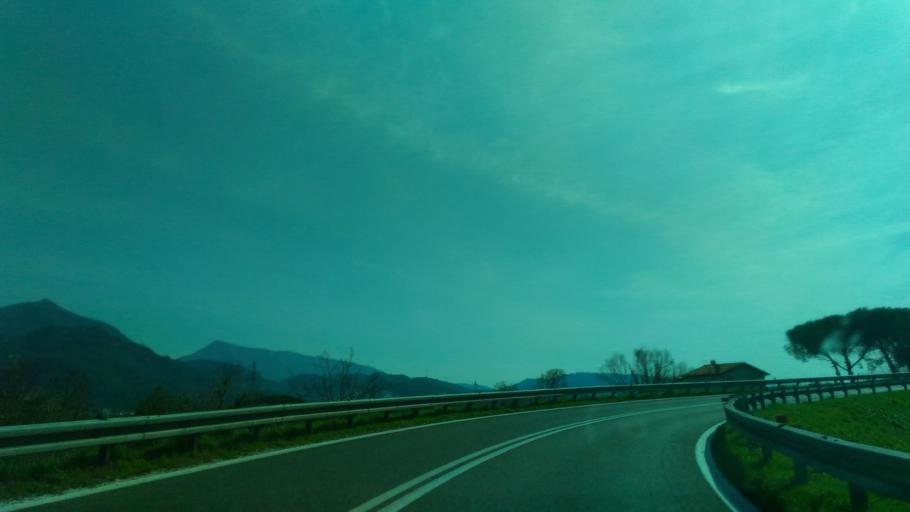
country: IT
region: Tuscany
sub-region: Provincia di Lucca
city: Pietrasanta
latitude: 43.9554
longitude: 10.2026
